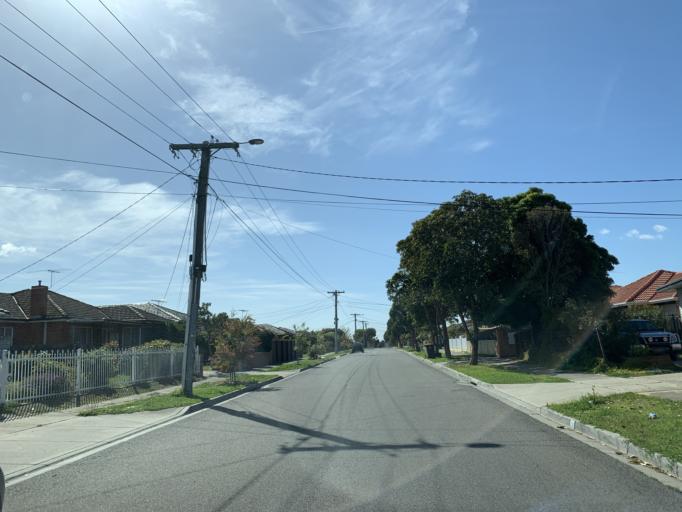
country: AU
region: Victoria
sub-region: Brimbank
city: Kealba
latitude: -37.7363
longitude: 144.8142
